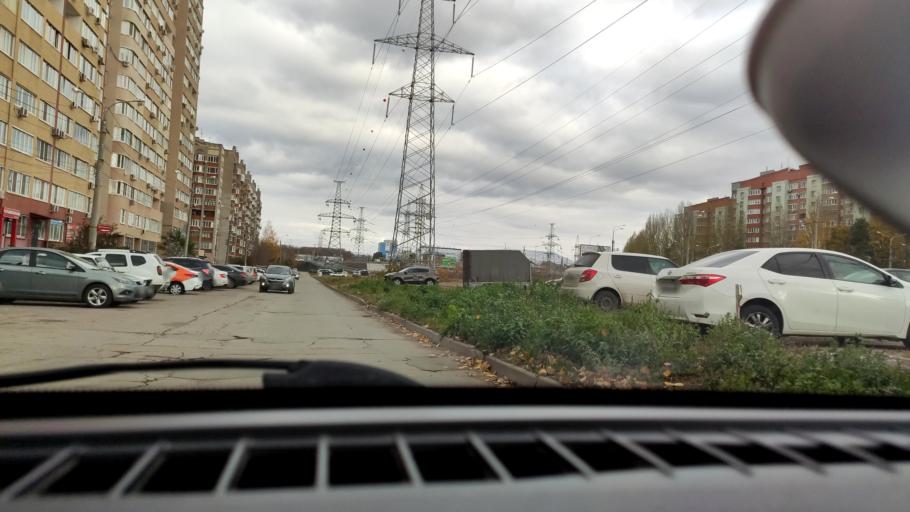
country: RU
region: Samara
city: Samara
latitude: 53.2662
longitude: 50.2185
